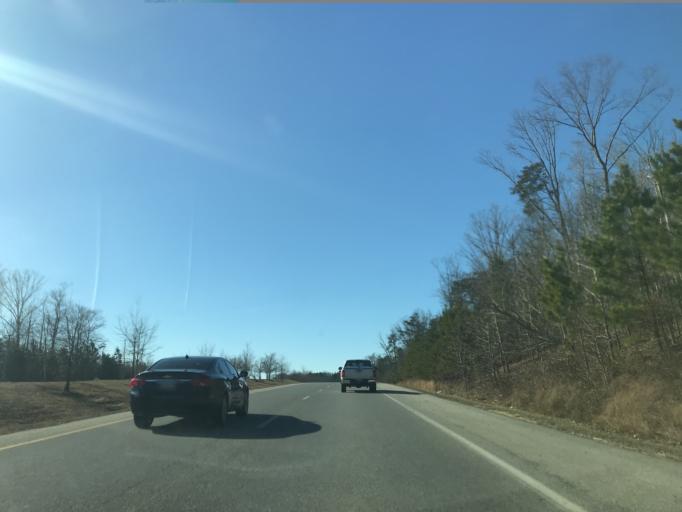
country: US
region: Maryland
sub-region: Charles County
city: Saint Charles
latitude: 38.5603
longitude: -76.9374
